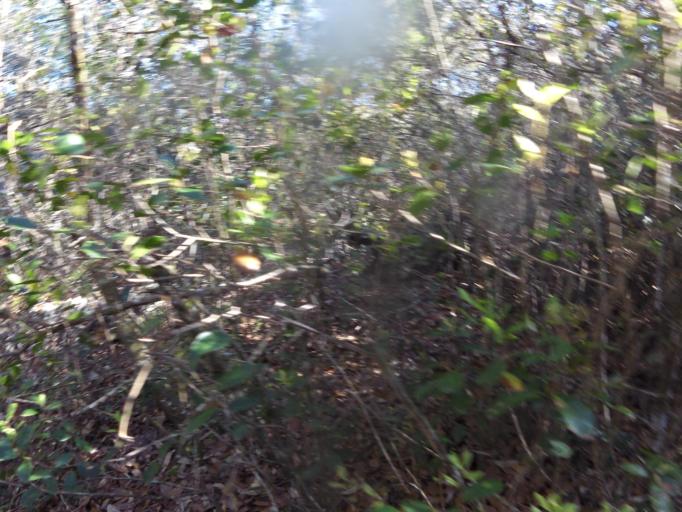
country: US
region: Florida
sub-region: Clay County
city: Keystone Heights
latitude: 29.8379
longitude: -81.9885
